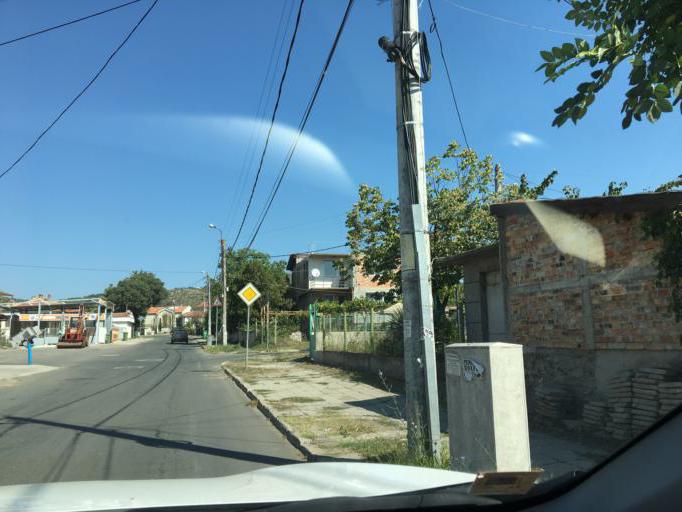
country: BG
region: Burgas
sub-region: Obshtina Kameno
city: Kameno
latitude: 42.6264
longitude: 27.3957
